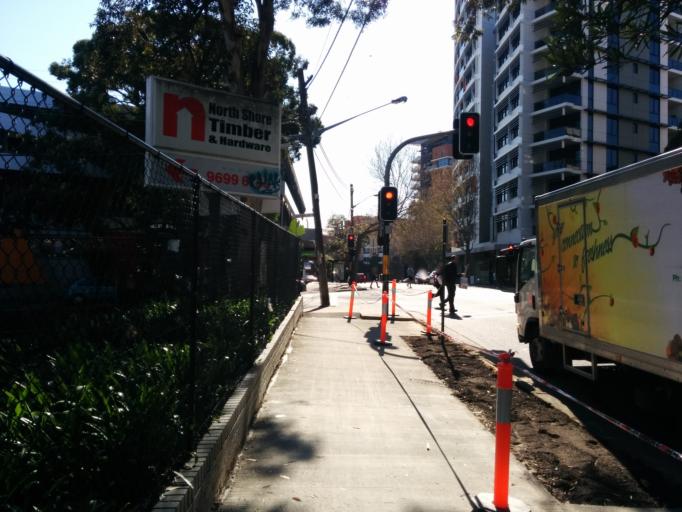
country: AU
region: New South Wales
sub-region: City of Sydney
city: Redfern
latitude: -33.8982
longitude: 151.2121
